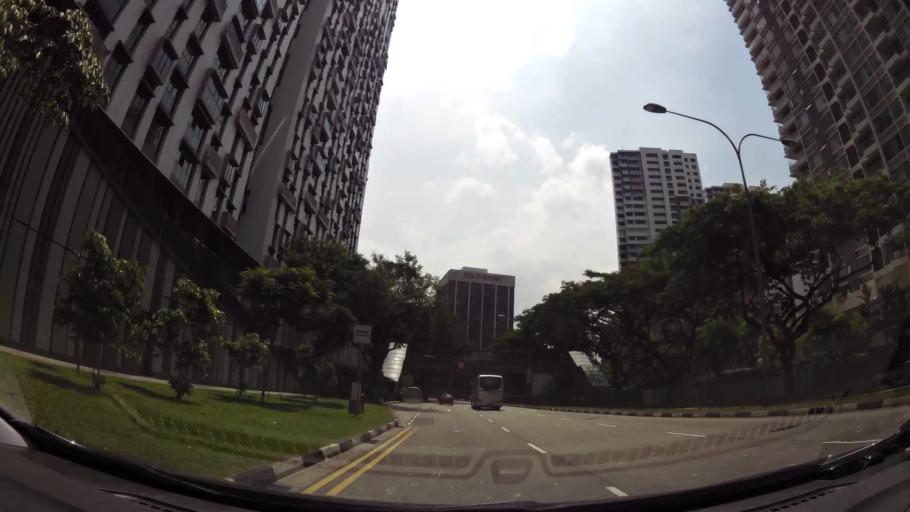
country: SG
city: Singapore
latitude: 1.2761
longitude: 103.8409
